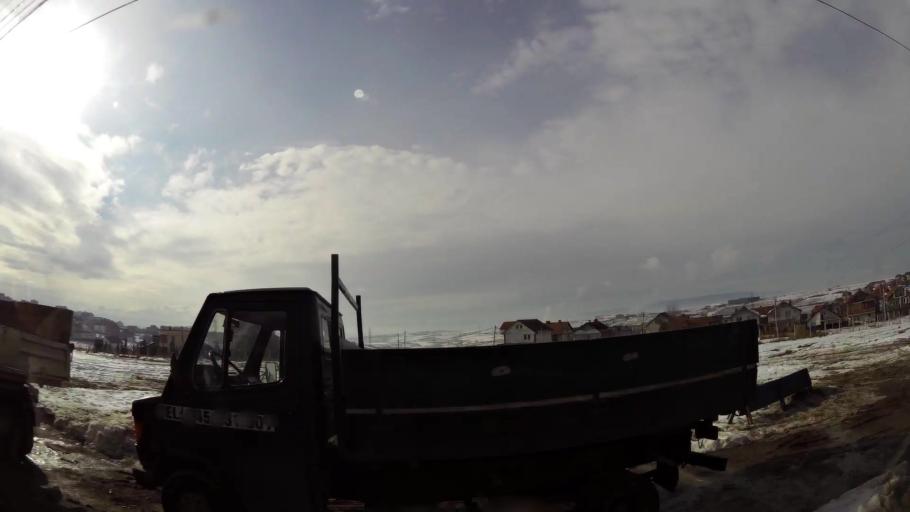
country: XK
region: Pristina
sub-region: Komuna e Prishtines
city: Pristina
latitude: 42.6892
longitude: 21.1563
